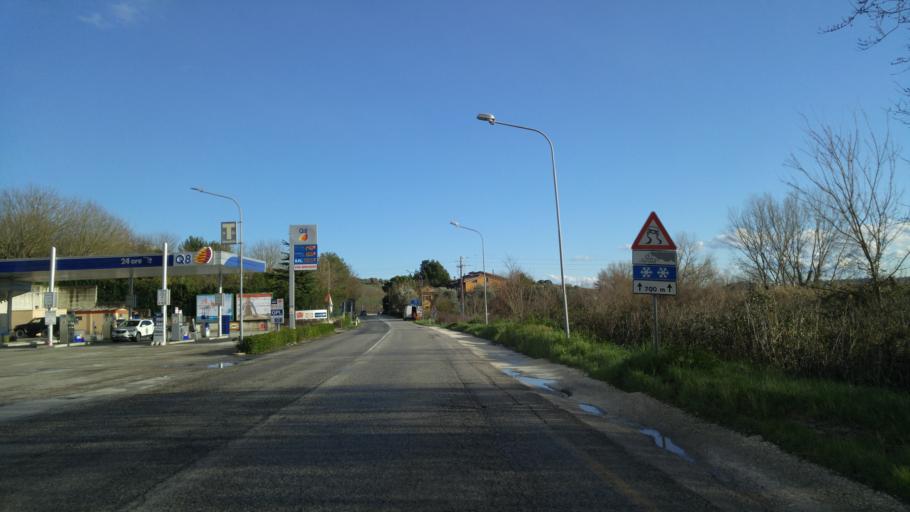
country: IT
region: The Marches
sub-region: Provincia di Ancona
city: Camerano
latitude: 43.5321
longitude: 13.5252
